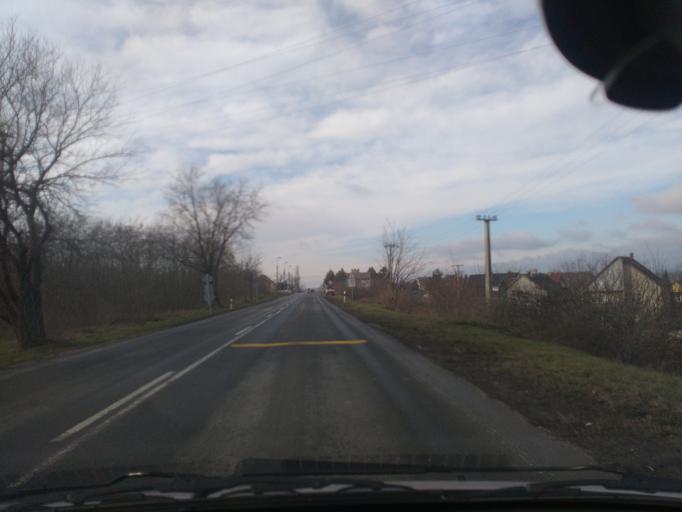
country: HU
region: Komarom-Esztergom
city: Dorog
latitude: 47.7306
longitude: 18.6980
